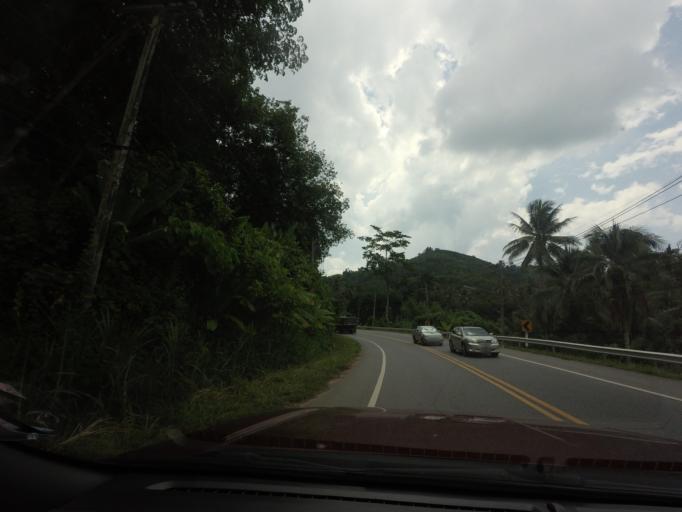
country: TH
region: Yala
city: Than To
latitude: 6.0751
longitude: 101.1917
